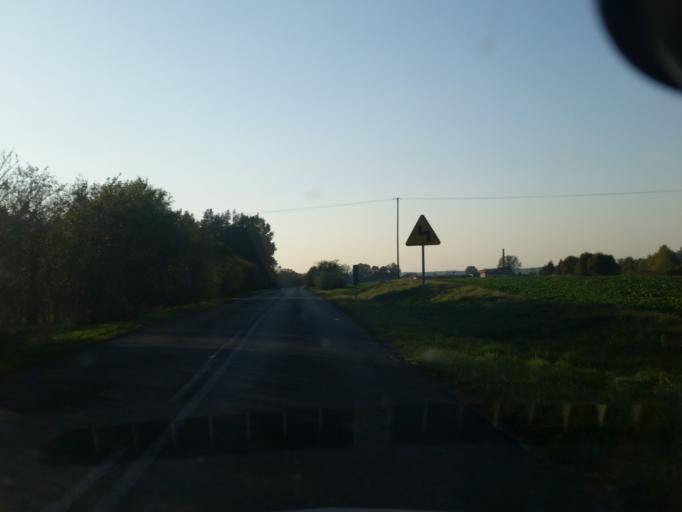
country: PL
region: Kujawsko-Pomorskie
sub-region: Powiat brodnicki
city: Gorzno
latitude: 53.2438
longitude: 19.6751
